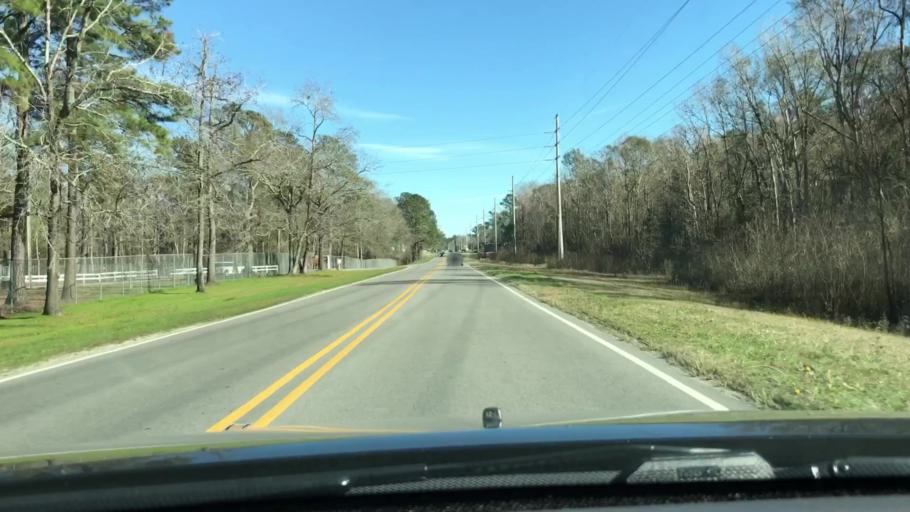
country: US
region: North Carolina
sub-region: Brunswick County
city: Shallotte
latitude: 33.9603
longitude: -78.4117
